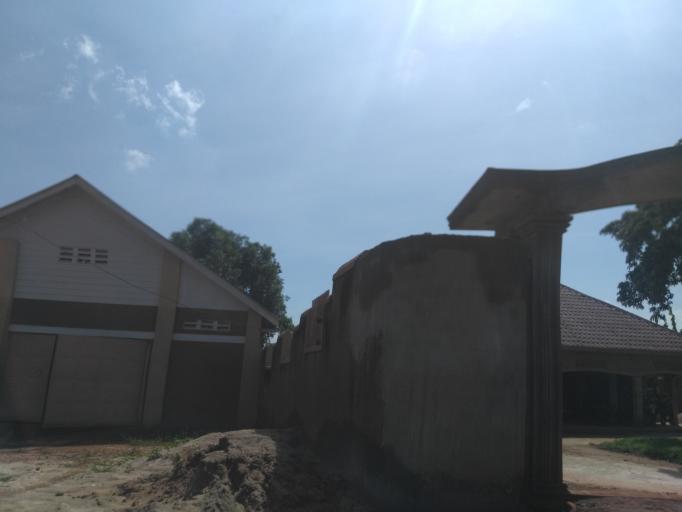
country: UG
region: Central Region
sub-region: Wakiso District
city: Kireka
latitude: 0.4533
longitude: 32.5829
